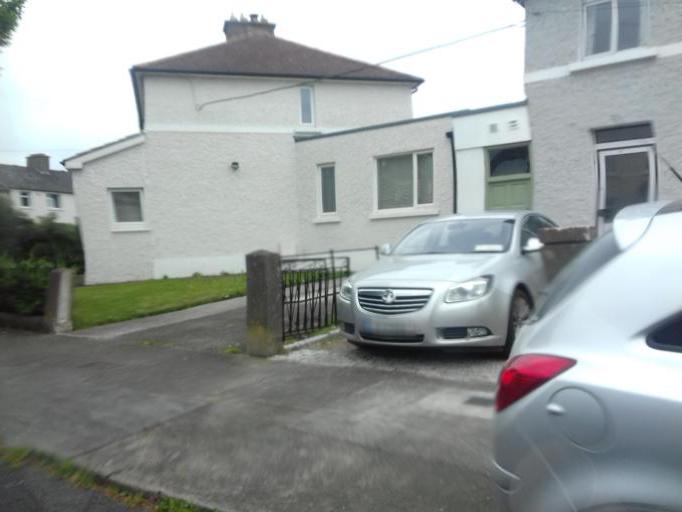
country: IE
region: Leinster
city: Glasnevin
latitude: 53.3741
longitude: -6.2606
